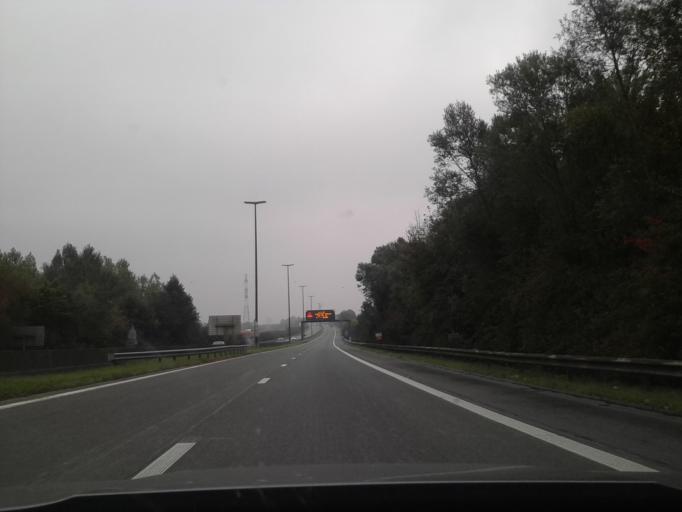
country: BE
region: Wallonia
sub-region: Province du Hainaut
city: Lessines
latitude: 50.6785
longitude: 3.8257
